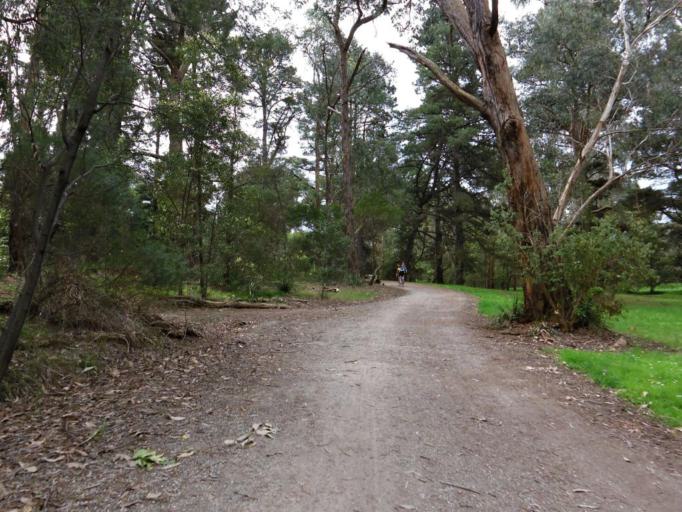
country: AU
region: Victoria
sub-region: Maroondah
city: Ringwood East
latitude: -37.7999
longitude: 145.2478
